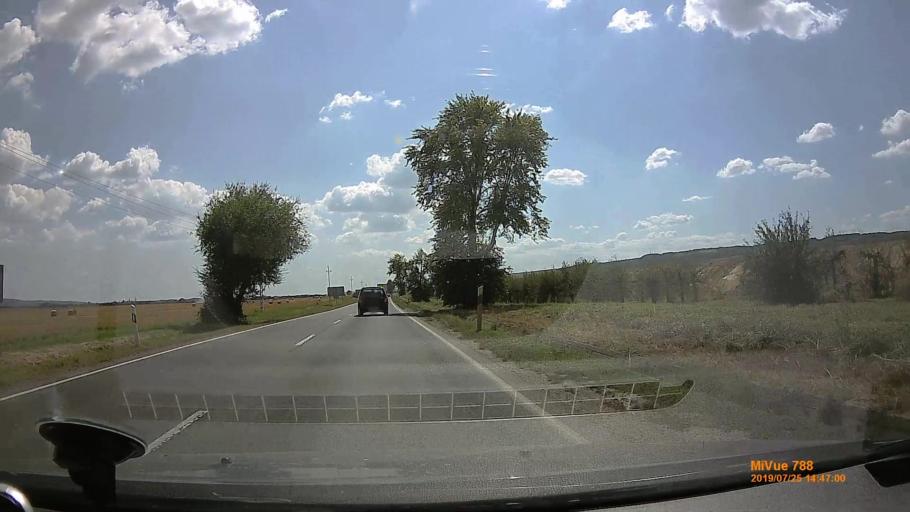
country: HU
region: Borsod-Abauj-Zemplen
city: Halmaj
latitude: 48.2508
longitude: 20.9785
